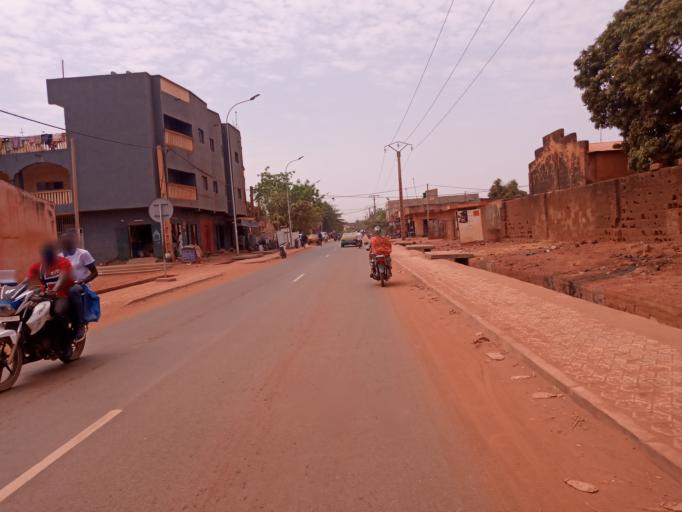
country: ML
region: Bamako
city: Bamako
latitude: 12.5826
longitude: -7.9882
